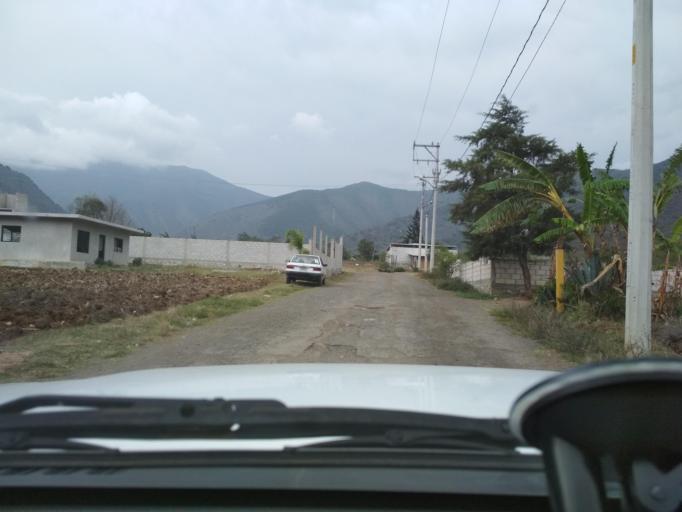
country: MX
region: Veracruz
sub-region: Nogales
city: Taza de Agua Ojo Zarco
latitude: 18.7889
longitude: -97.2121
